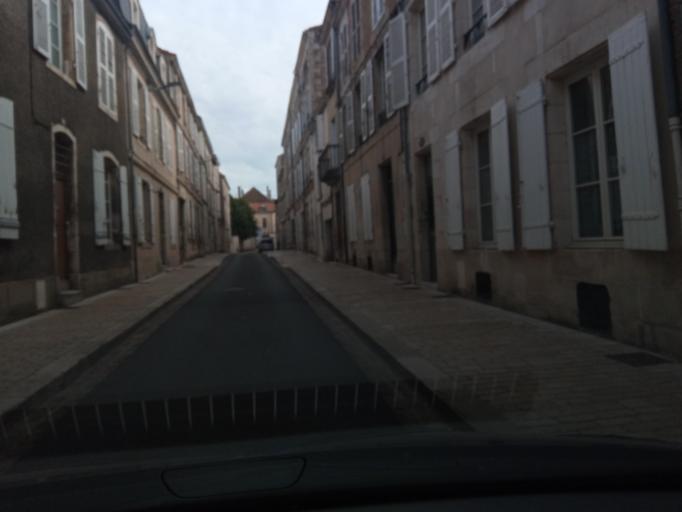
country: FR
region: Poitou-Charentes
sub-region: Departement de la Vienne
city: Poitiers
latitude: 46.5755
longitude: 0.3321
